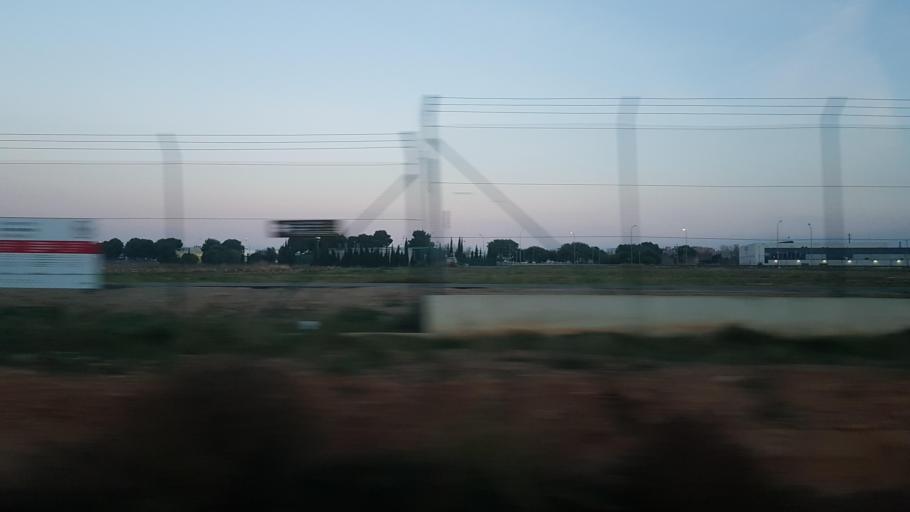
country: ES
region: Valencia
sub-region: Provincia de Valencia
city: Manises
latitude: 39.4814
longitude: -0.4610
